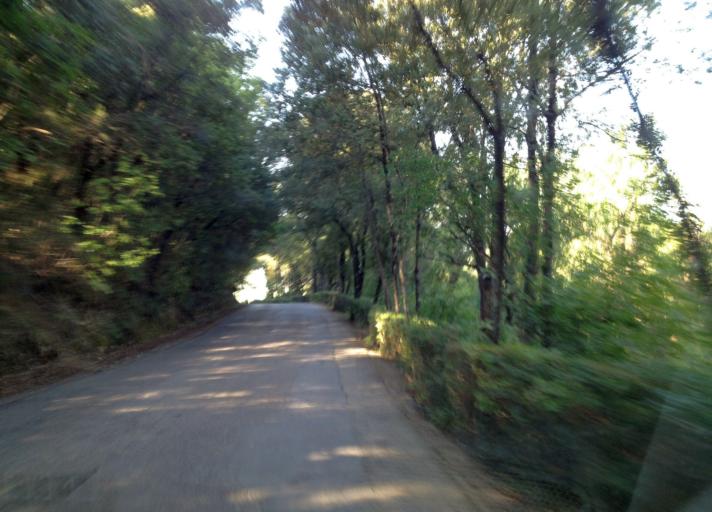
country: IT
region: Tuscany
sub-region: Provincia di Siena
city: Poggibonsi
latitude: 43.4923
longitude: 11.1838
